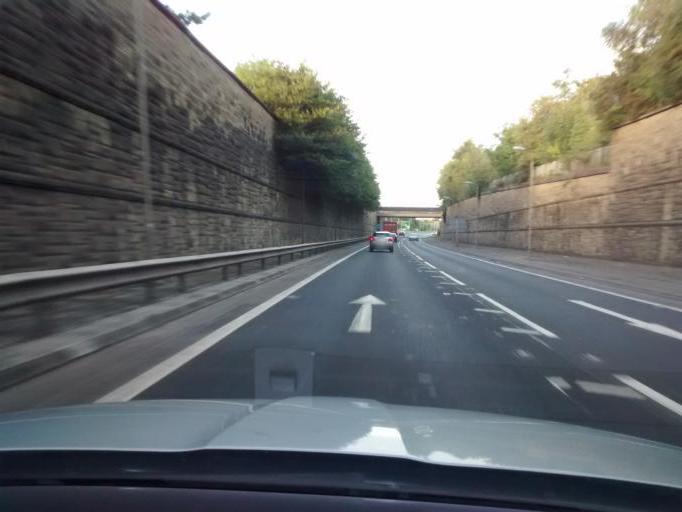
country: GB
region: Scotland
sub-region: Renfrewshire
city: Kilbarchan
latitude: 55.8295
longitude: -4.5369
